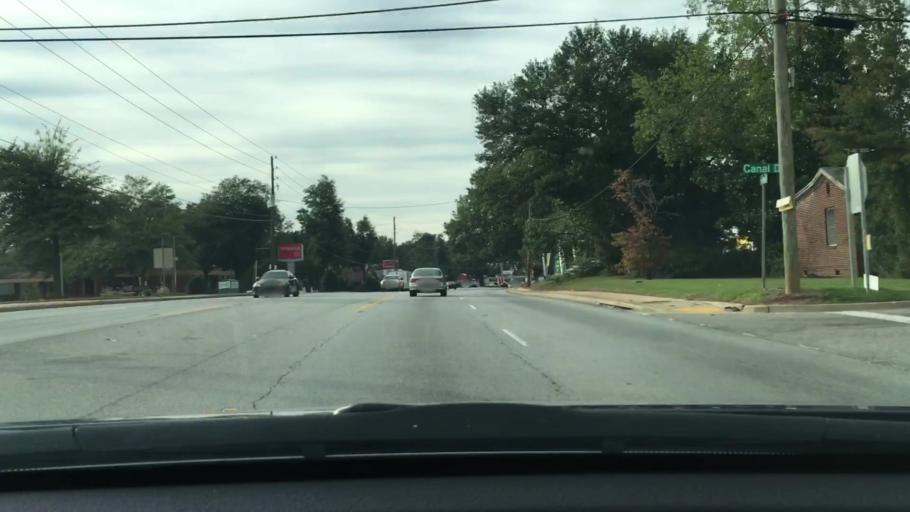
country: US
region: South Carolina
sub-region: Lexington County
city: West Columbia
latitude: 34.0255
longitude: -81.0806
